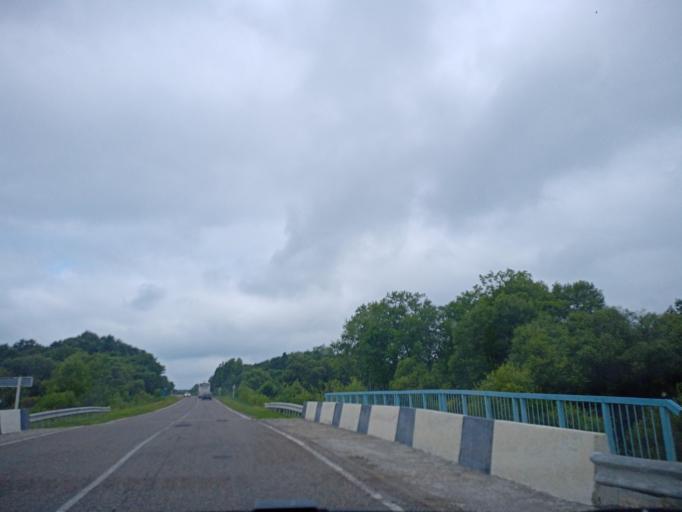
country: RU
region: Primorskiy
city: Novopokrovka
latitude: 45.9709
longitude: 134.2345
